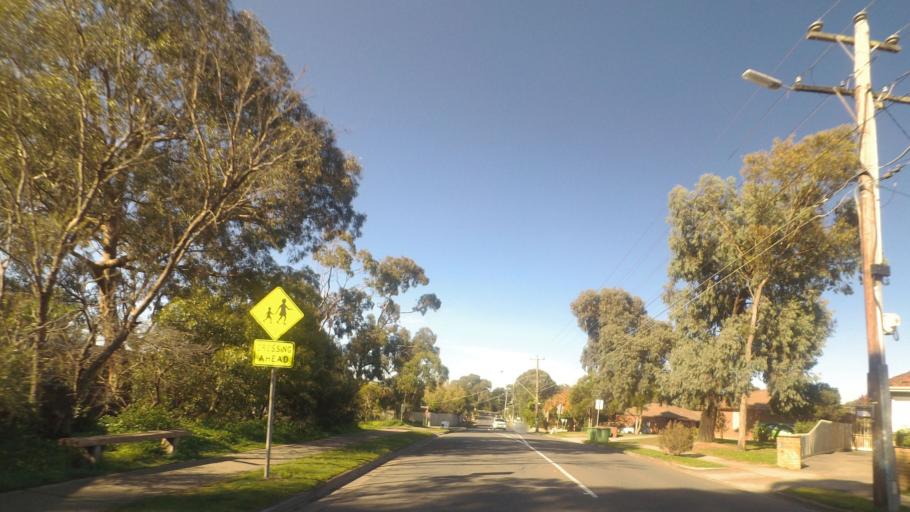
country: AU
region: Victoria
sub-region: Banyule
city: Montmorency
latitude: -37.7176
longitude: 145.1229
